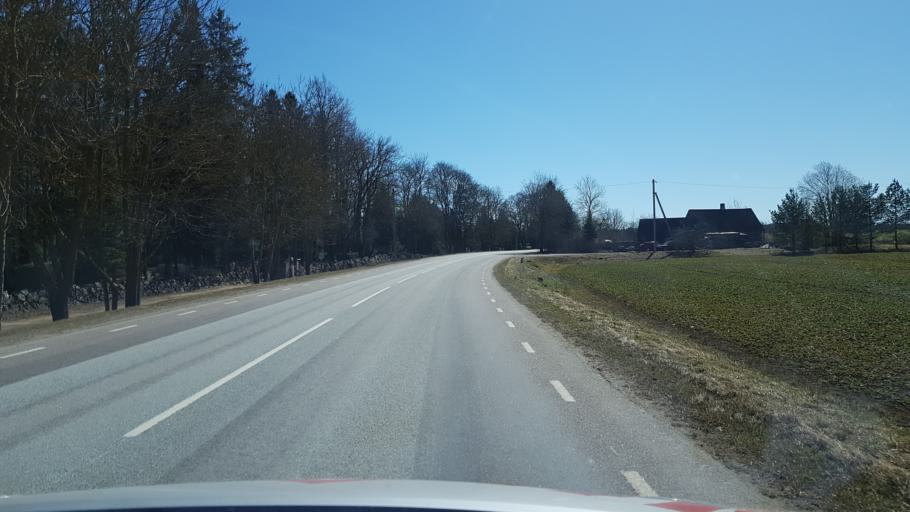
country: EE
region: Ida-Virumaa
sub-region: Aseri vald
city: Aseri
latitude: 59.4373
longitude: 26.6986
